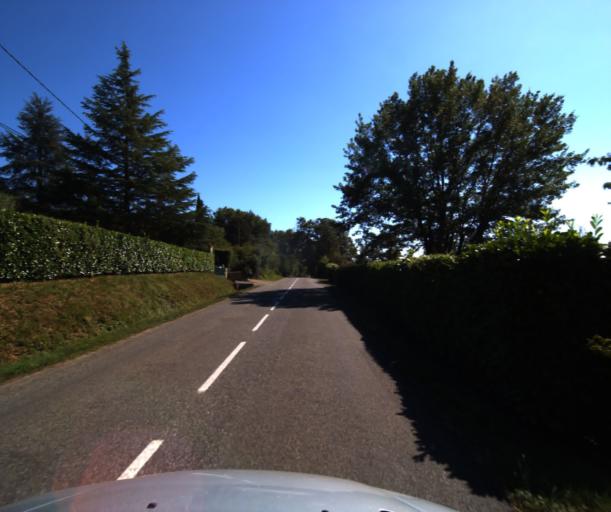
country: FR
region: Midi-Pyrenees
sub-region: Departement de la Haute-Garonne
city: Eaunes
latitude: 43.4299
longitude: 1.3237
